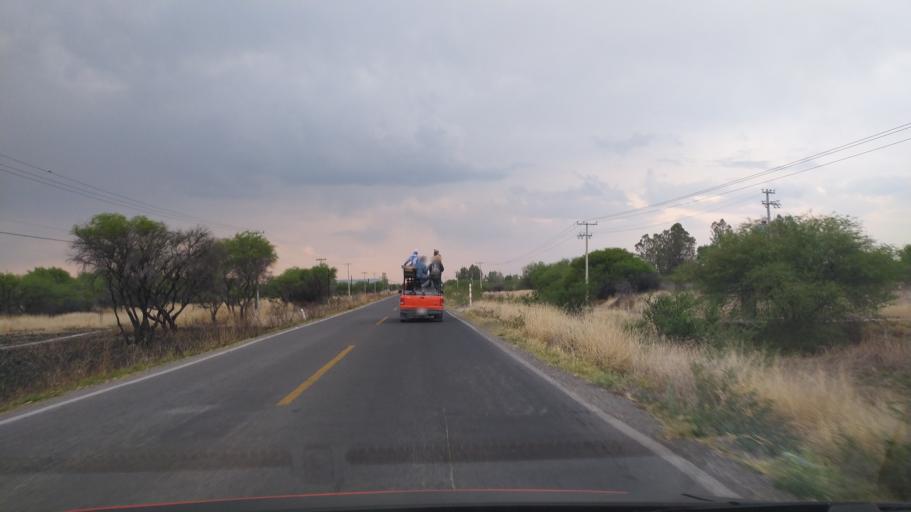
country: MX
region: Guanajuato
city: Ciudad Manuel Doblado
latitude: 20.8023
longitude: -101.9054
